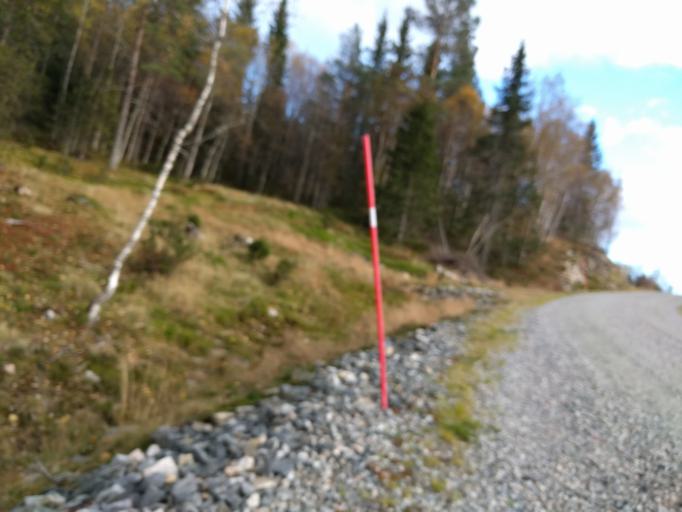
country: NO
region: Aust-Agder
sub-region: Evje og Hornnes
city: Evje
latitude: 58.6544
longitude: 7.9451
